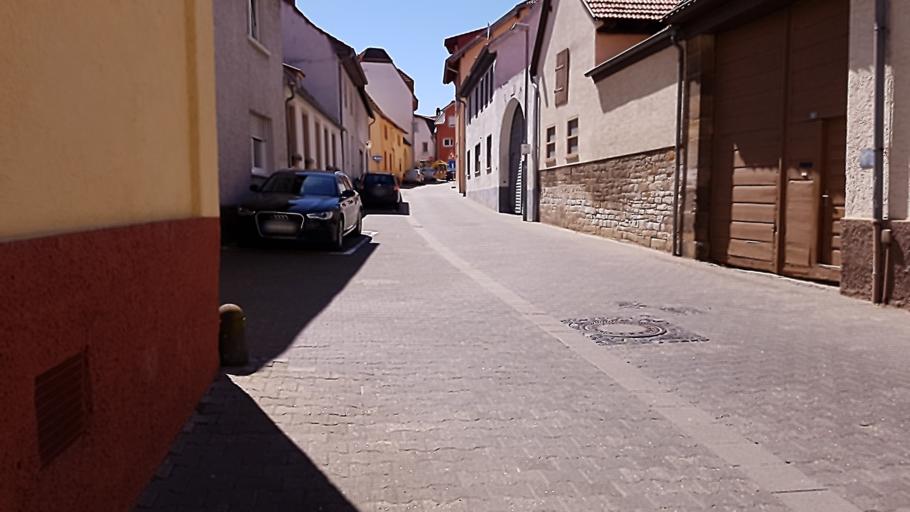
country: DE
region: Rheinland-Pfalz
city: Worrstadt
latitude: 49.8402
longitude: 8.1162
